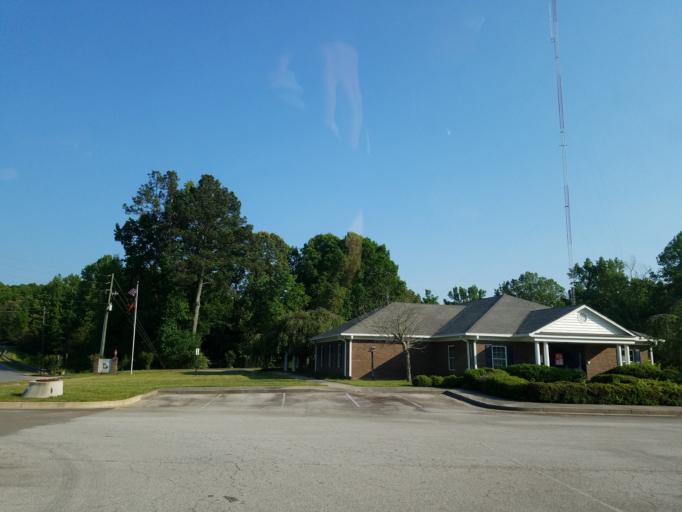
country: US
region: Georgia
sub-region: Forsyth County
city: Cumming
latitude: 34.2692
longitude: -84.0846
